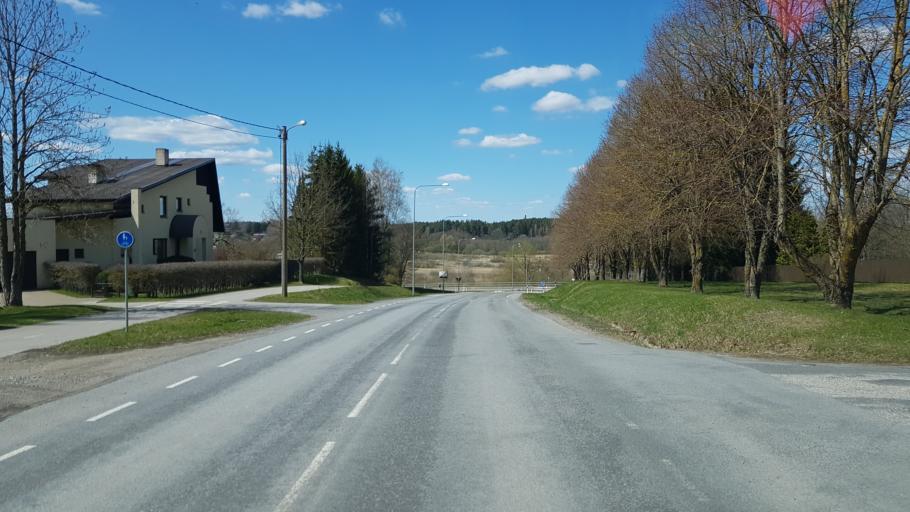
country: EE
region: Viljandimaa
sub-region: Viiratsi vald
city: Viiratsi
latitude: 58.3623
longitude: 25.6406
